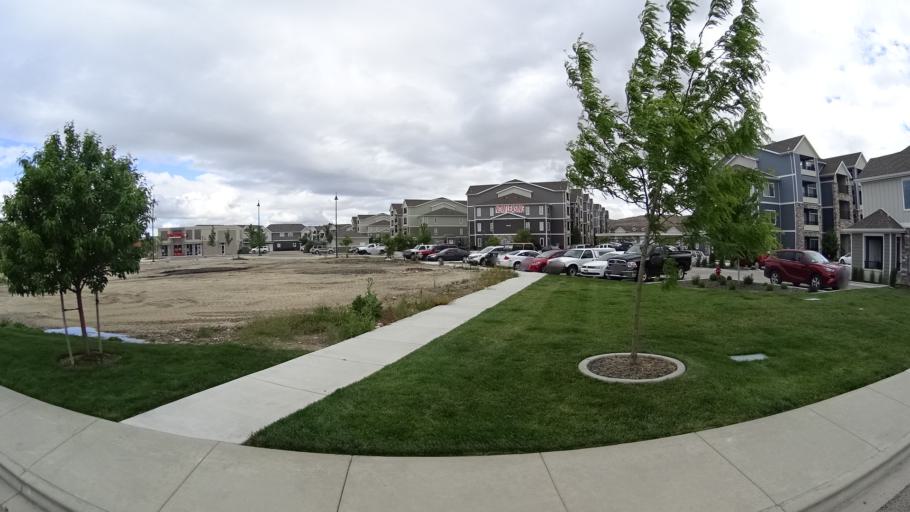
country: US
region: Idaho
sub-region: Ada County
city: Garden City
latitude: 43.6710
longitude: -116.2811
